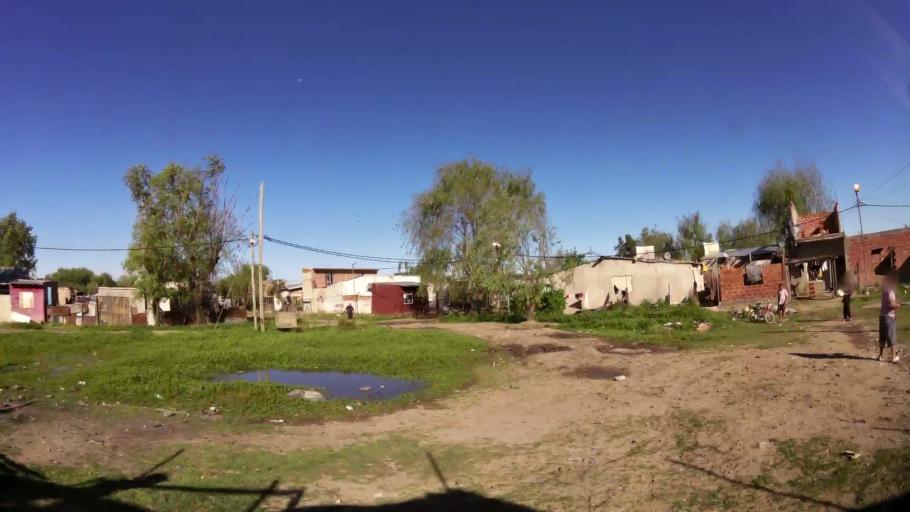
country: AR
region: Buenos Aires
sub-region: Partido de Quilmes
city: Quilmes
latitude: -34.7540
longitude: -58.3195
